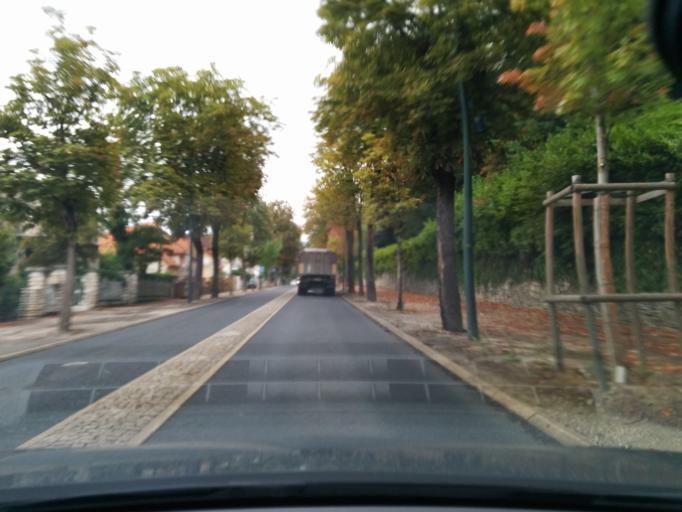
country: FR
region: Midi-Pyrenees
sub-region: Departement du Lot
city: Souillac
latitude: 44.8887
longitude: 1.4829
